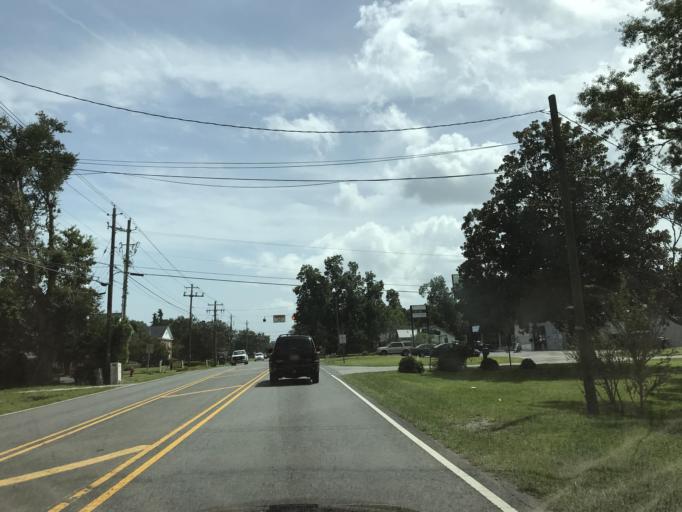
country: US
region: North Carolina
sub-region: New Hanover County
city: Wrightsboro
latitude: 34.2947
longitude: -77.9213
